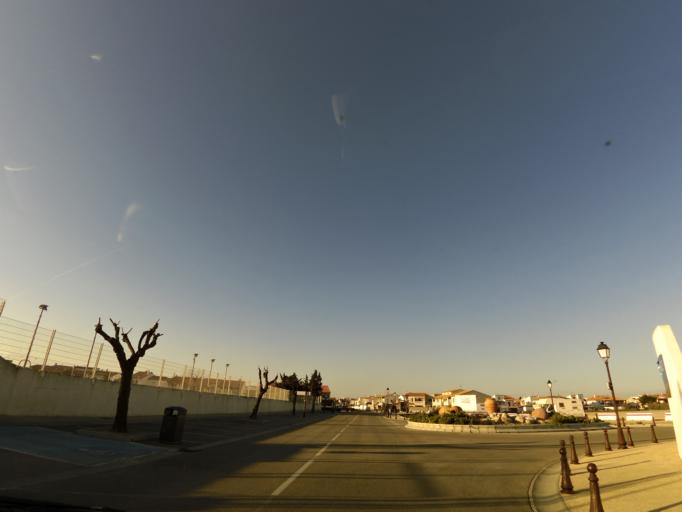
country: FR
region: Provence-Alpes-Cote d'Azur
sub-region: Departement des Bouches-du-Rhone
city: Saintes-Maries-de-la-Mer
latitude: 43.4534
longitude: 4.4337
